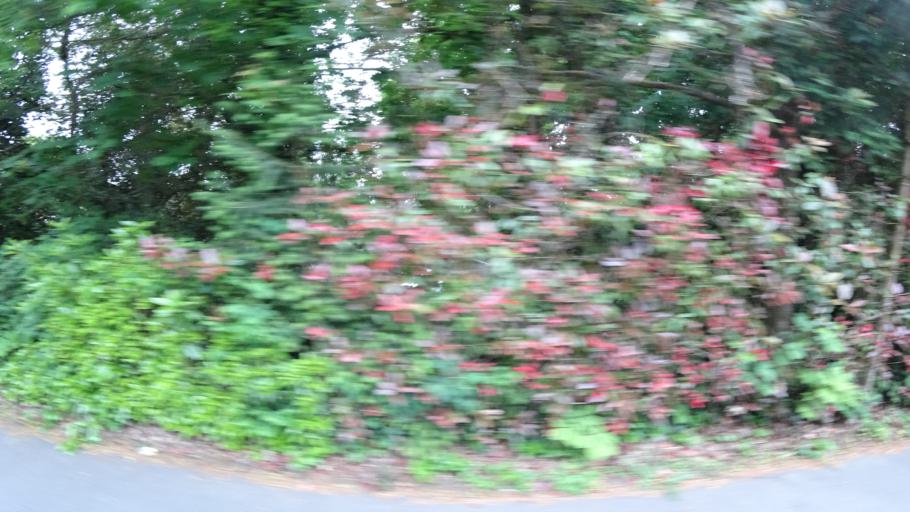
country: US
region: Oregon
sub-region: Multnomah County
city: Portland
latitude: 45.4879
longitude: -122.7022
